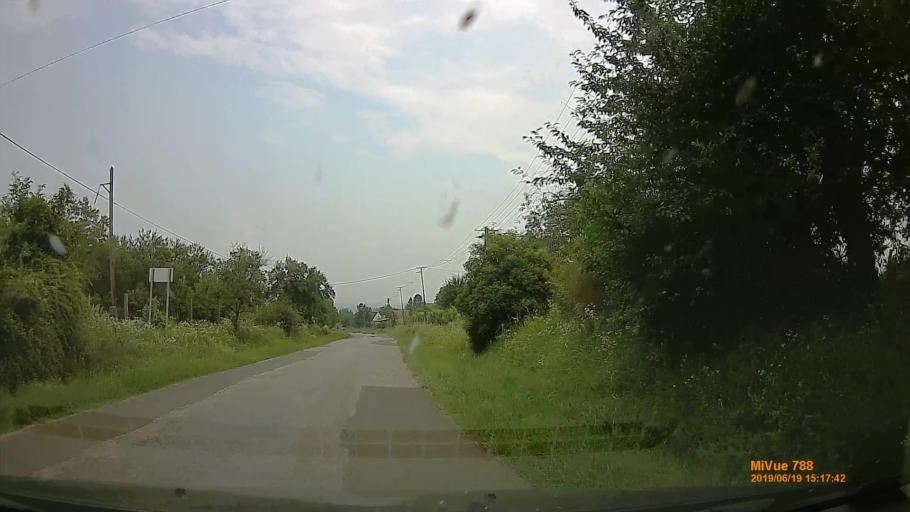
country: HU
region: Baranya
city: Szigetvar
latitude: 46.0793
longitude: 17.8494
